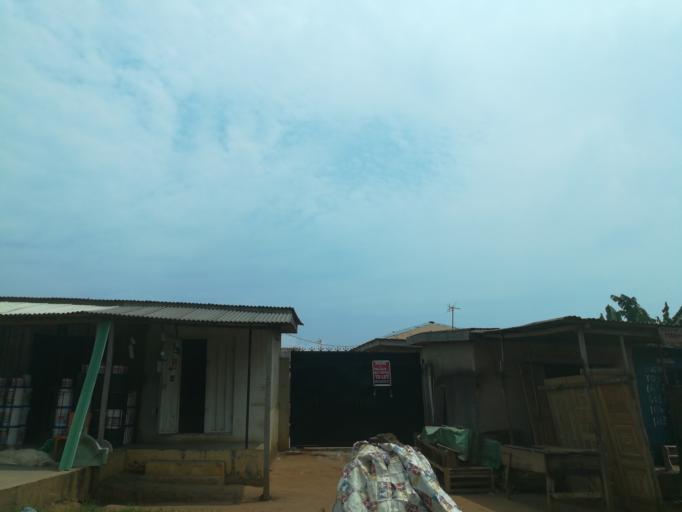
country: NG
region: Lagos
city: Ikorodu
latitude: 6.6072
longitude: 3.5868
